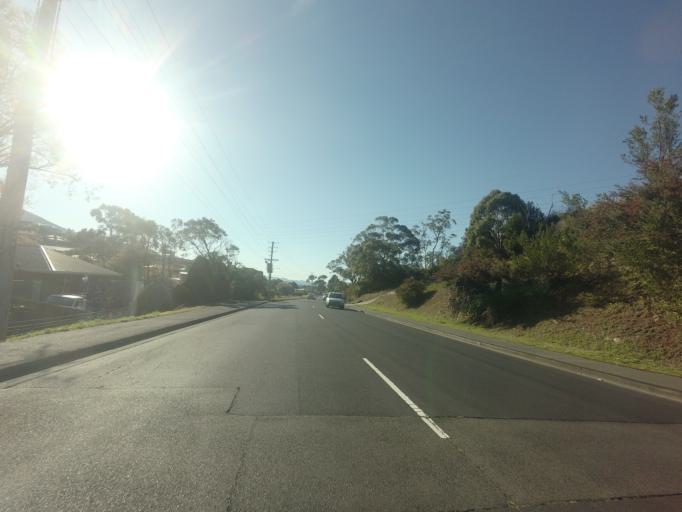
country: AU
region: Tasmania
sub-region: Glenorchy
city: West Moonah
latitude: -42.8521
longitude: 147.2681
